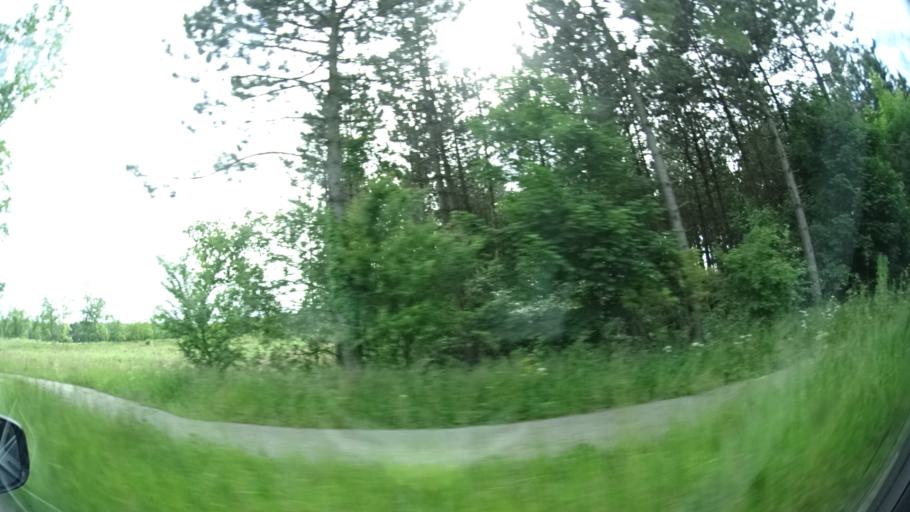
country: DK
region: Central Jutland
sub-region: Norddjurs Kommune
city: Grenaa
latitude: 56.5007
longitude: 10.7380
